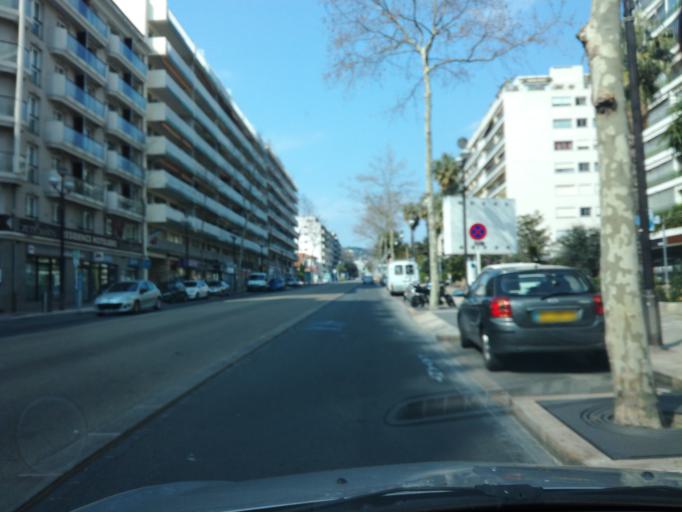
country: FR
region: Provence-Alpes-Cote d'Azur
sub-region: Departement des Alpes-Maritimes
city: Cannes
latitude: 43.5620
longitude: 7.0168
